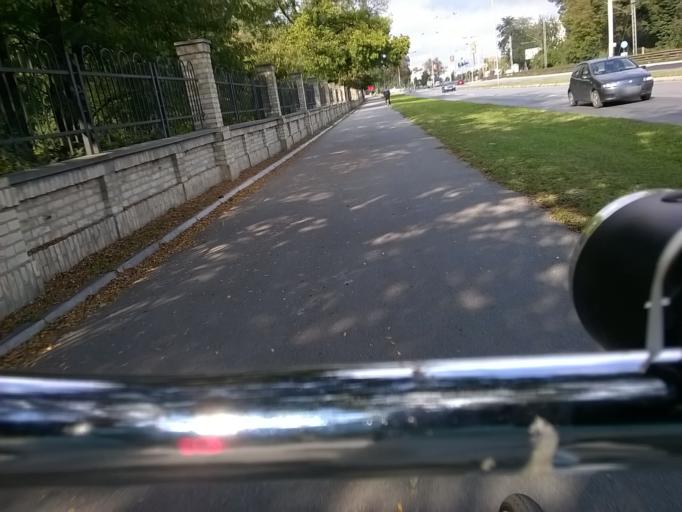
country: RS
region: Autonomna Pokrajina Vojvodina
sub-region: Juznobanatski Okrug
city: Pancevo
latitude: 44.8632
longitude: 20.6580
